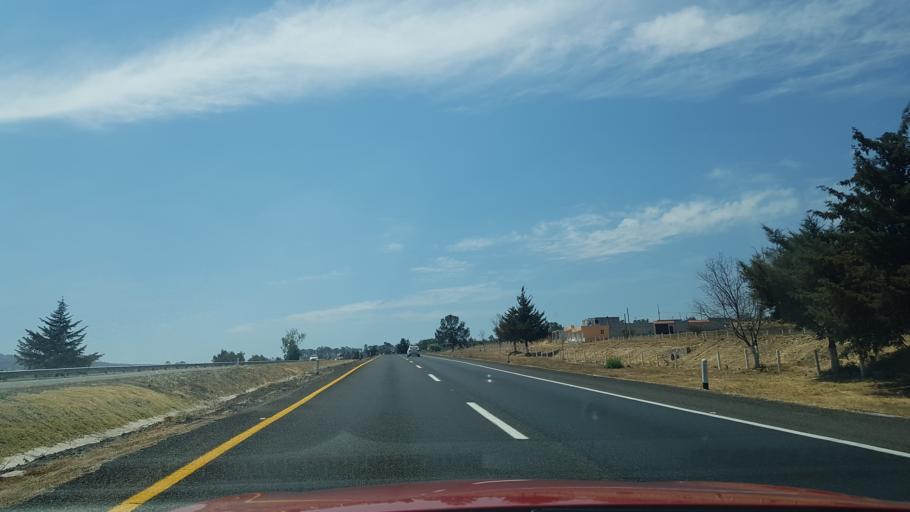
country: MX
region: Michoacan
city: Maravatio
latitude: 19.9108
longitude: -100.4706
